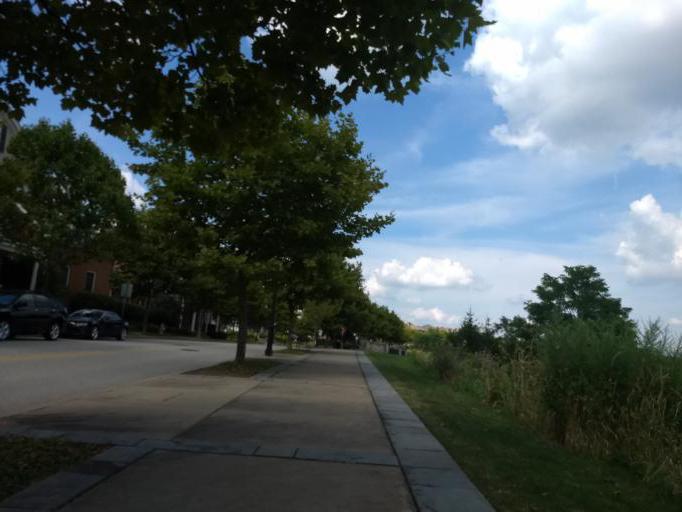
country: US
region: Pennsylvania
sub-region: Allegheny County
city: Homestead
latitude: 40.4187
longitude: -79.9167
